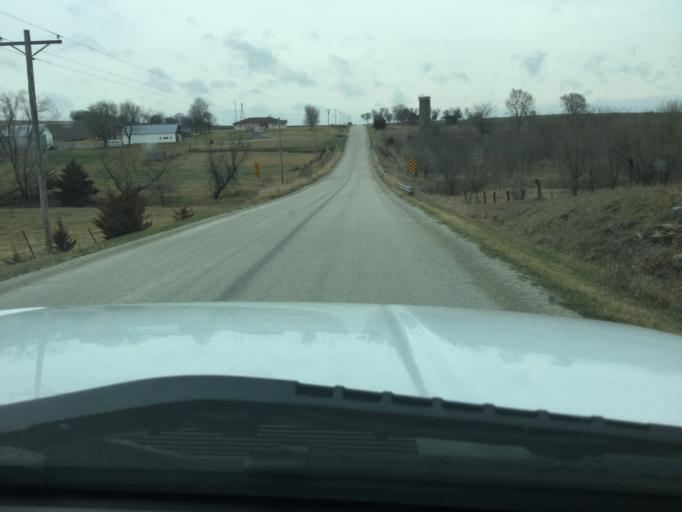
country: US
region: Kansas
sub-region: Nemaha County
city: Sabetha
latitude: 39.8786
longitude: -95.7142
